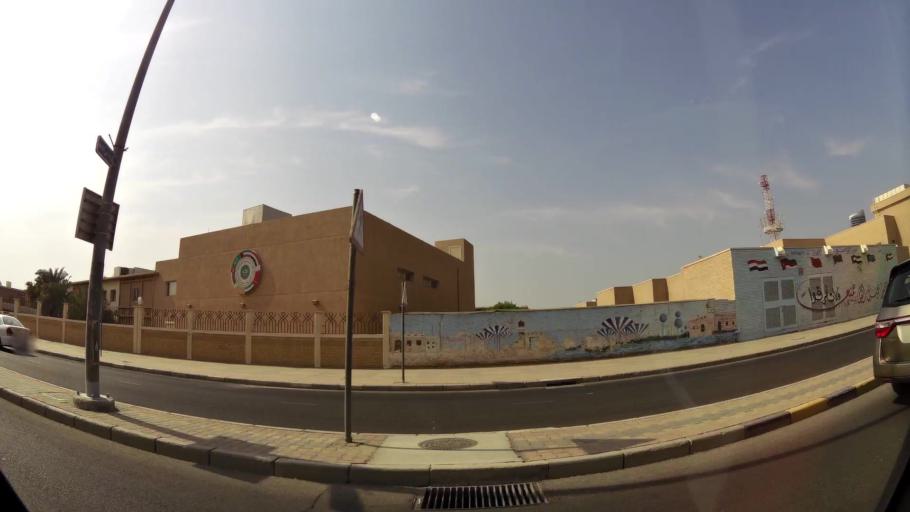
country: KW
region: Al Asimah
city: Ash Shamiyah
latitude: 29.3535
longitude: 47.9655
